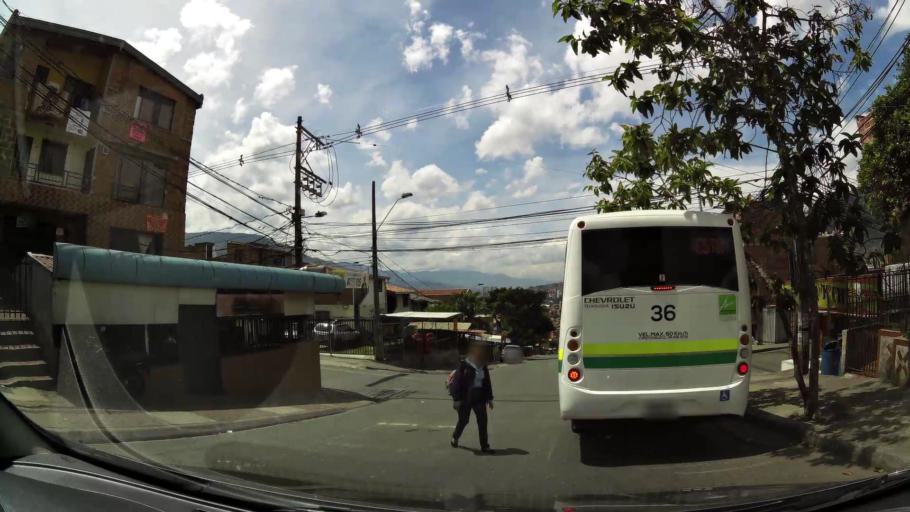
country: CO
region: Antioquia
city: Bello
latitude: 6.3467
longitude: -75.5547
